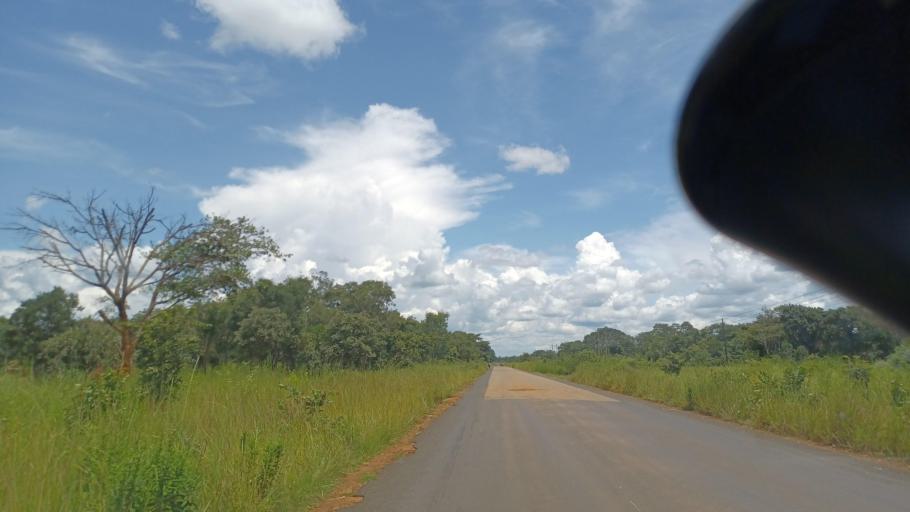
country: ZM
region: North-Western
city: Solwezi
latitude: -12.5677
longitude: 26.1375
